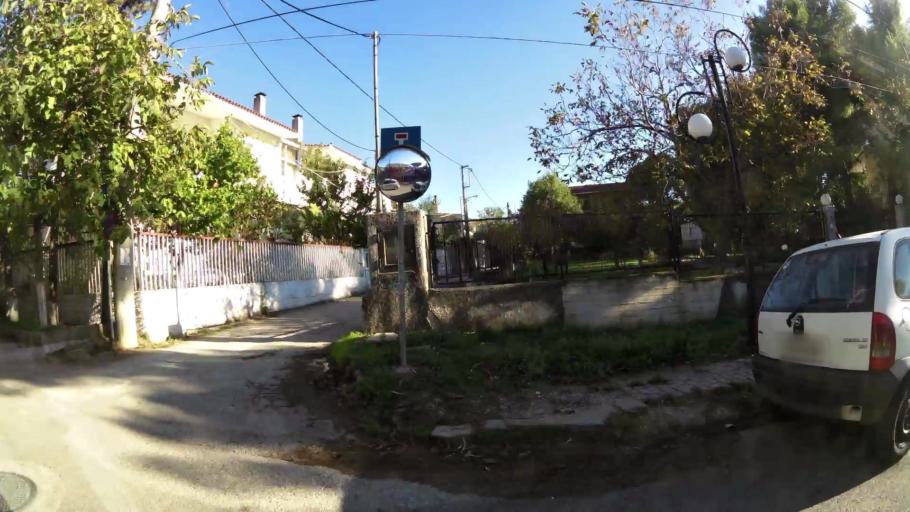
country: GR
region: Attica
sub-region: Nomarchia Anatolikis Attikis
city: Anoixi
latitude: 38.1339
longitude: 23.8570
